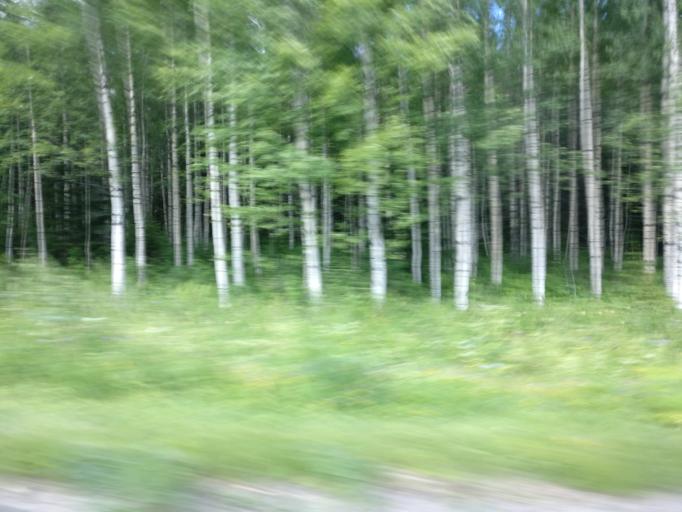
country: FI
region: Southern Savonia
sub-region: Savonlinna
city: Kerimaeki
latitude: 61.8421
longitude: 29.2051
